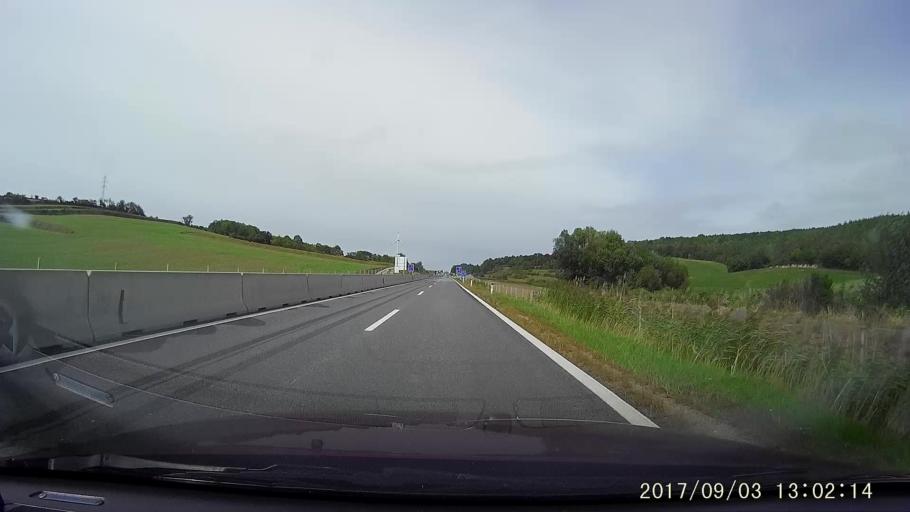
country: AT
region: Lower Austria
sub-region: Politischer Bezirk Hollabrunn
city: Hollabrunn
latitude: 48.5176
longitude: 16.0863
